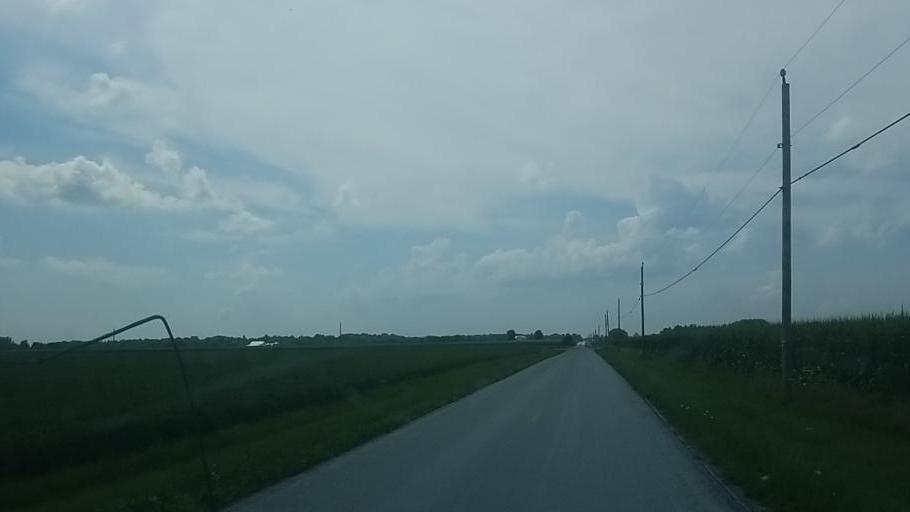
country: US
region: Ohio
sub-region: Hardin County
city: Kenton
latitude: 40.7030
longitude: -83.5901
